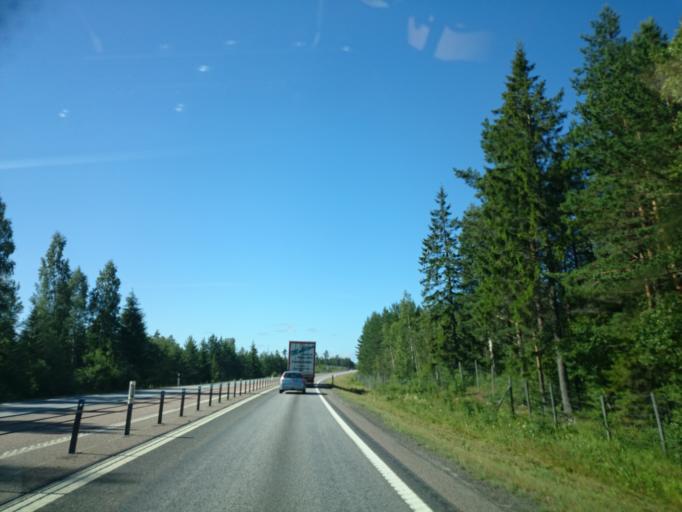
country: SE
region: Gaevleborg
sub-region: Soderhamns Kommun
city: Ljusne
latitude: 61.1110
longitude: 17.0091
